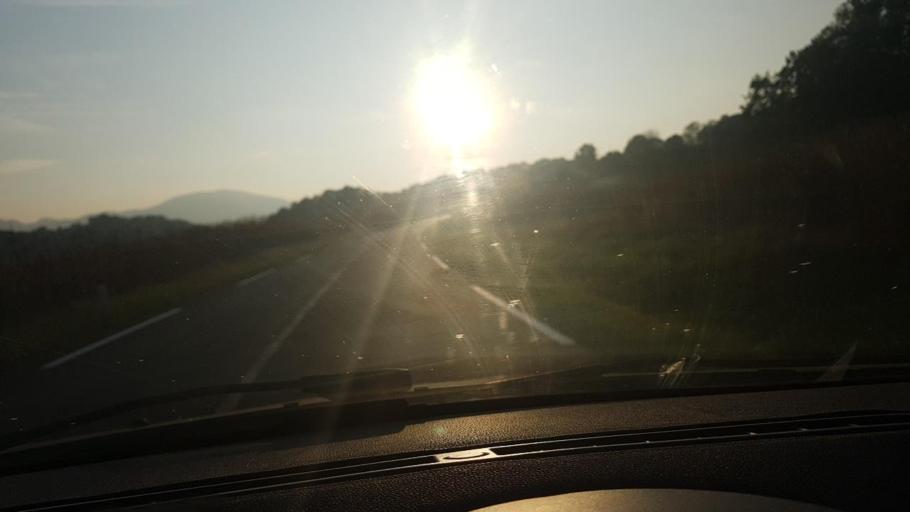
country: SI
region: Majsperk
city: Majsperk
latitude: 46.3362
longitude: 15.7035
